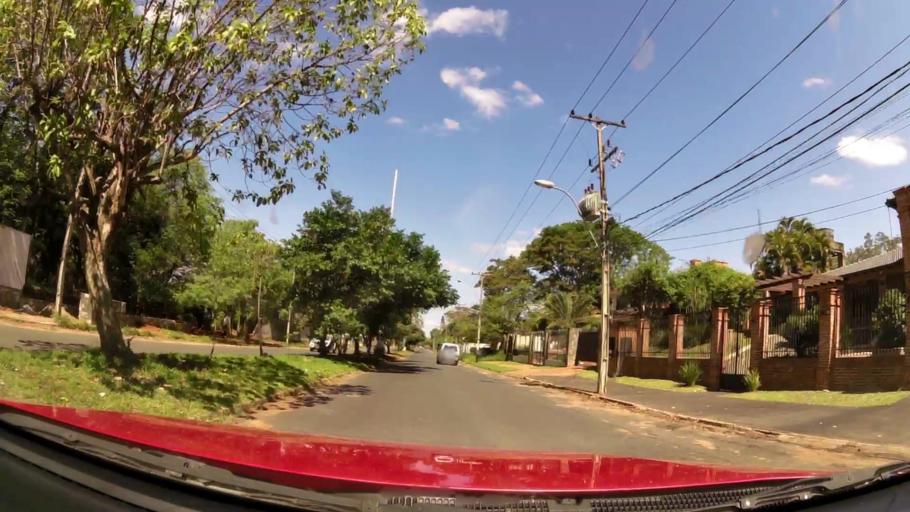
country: PY
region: Central
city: Fernando de la Mora
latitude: -25.2641
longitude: -57.5569
